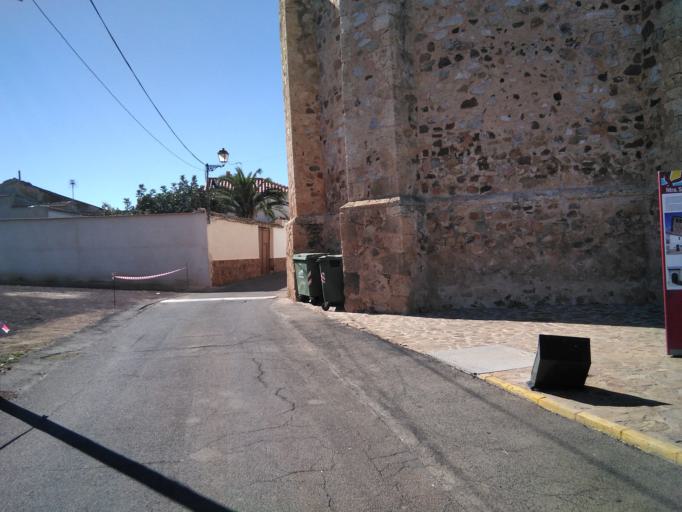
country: ES
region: Castille-La Mancha
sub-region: Provincia de Ciudad Real
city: Ballesteros de Calatrava
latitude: 38.8378
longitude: -3.9431
